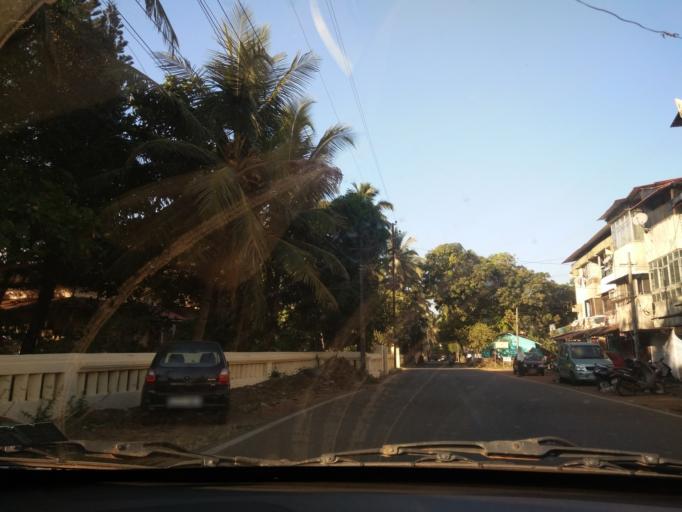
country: IN
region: Goa
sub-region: South Goa
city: Madgaon
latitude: 15.2551
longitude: 73.9640
